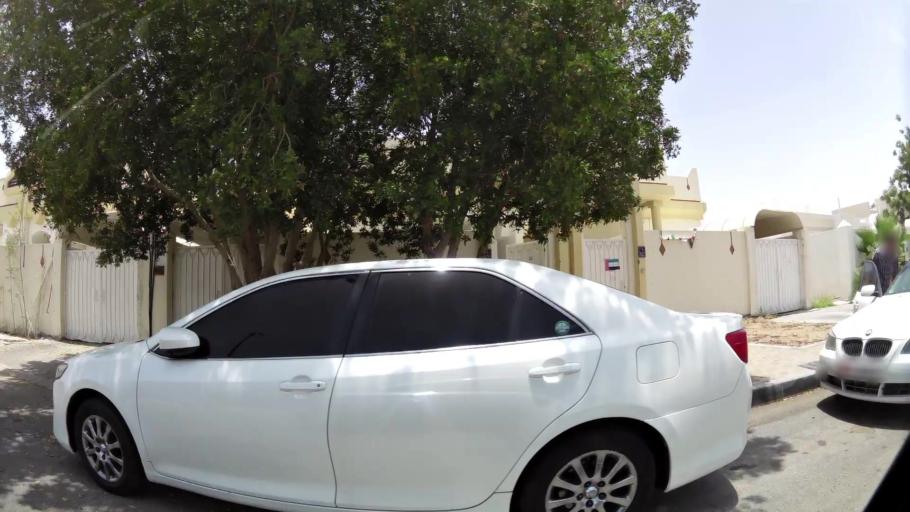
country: AE
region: Abu Dhabi
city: Al Ain
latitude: 24.2195
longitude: 55.7347
